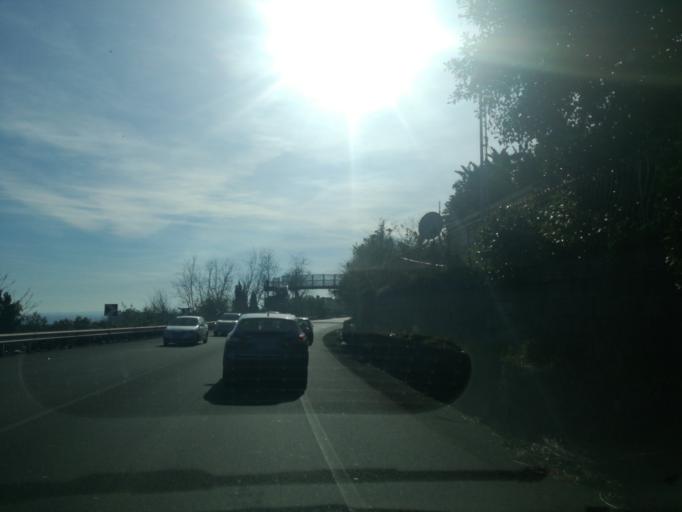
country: IT
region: Sicily
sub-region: Catania
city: Acireale
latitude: 37.6132
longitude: 15.1711
